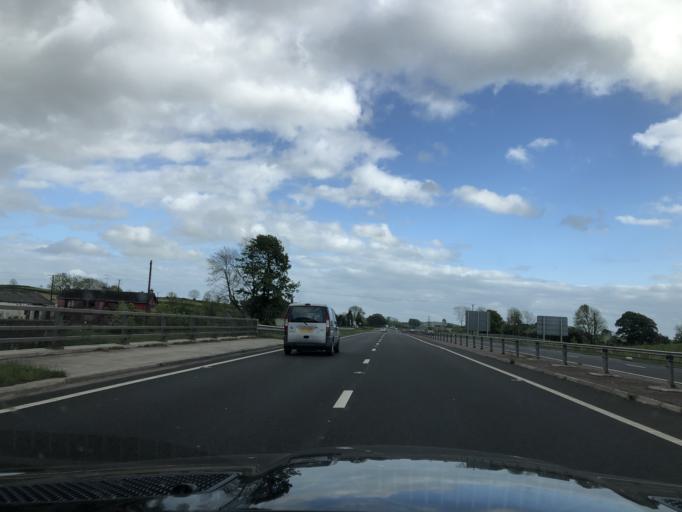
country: GB
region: Northern Ireland
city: Dunloy
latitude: 54.9980
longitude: -6.3542
